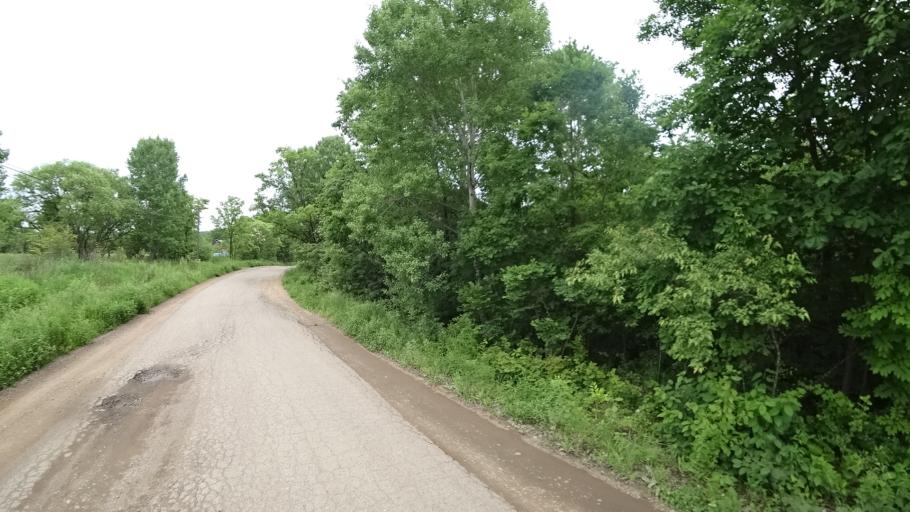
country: RU
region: Primorskiy
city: Novosysoyevka
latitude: 44.2029
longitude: 133.3220
